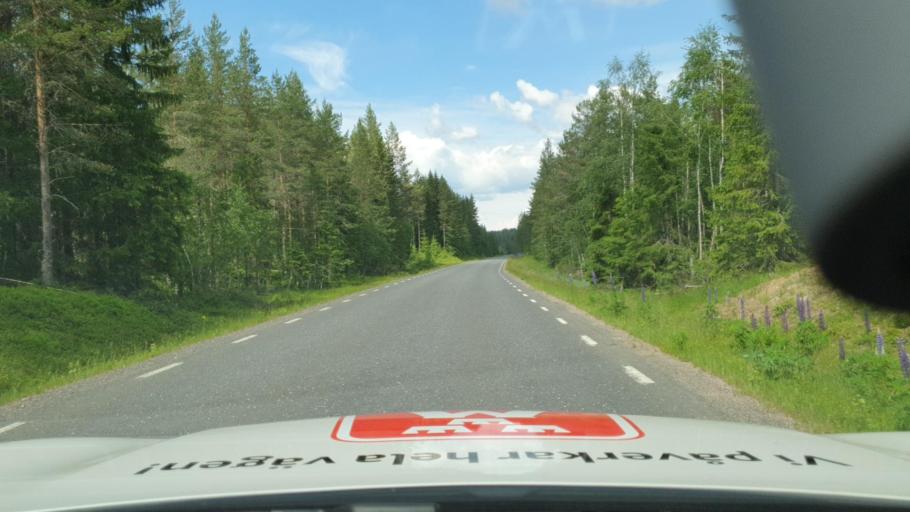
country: SE
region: Vaermland
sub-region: Torsby Kommun
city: Torsby
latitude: 60.5157
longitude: 12.8301
